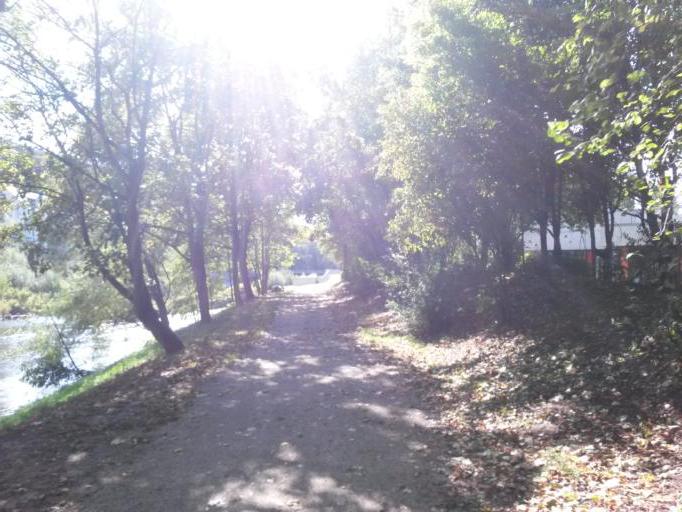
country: DE
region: Baden-Wuerttemberg
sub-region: Karlsruhe Region
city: Eutingen
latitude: 48.9090
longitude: 8.7486
